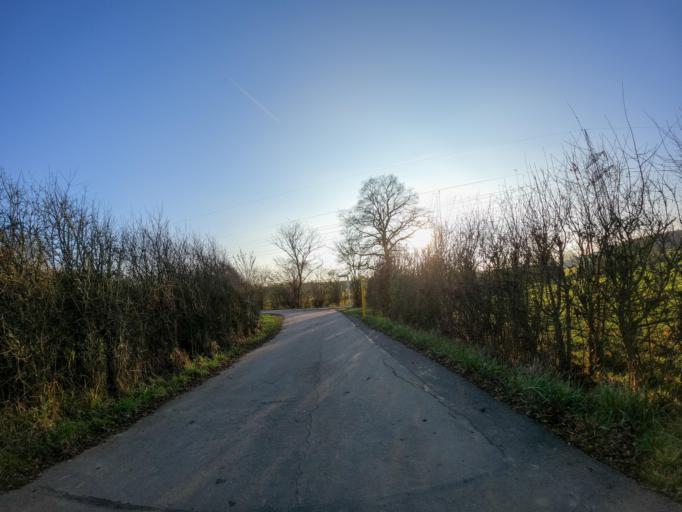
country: LU
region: Luxembourg
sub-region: Canton de Capellen
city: Mamer
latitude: 49.6106
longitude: 6.0313
